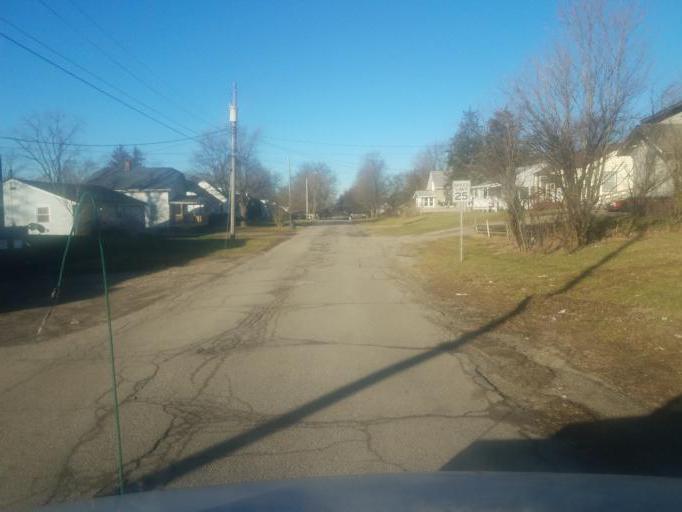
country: US
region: Ohio
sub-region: Richland County
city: Mansfield
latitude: 40.7845
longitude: -82.5497
